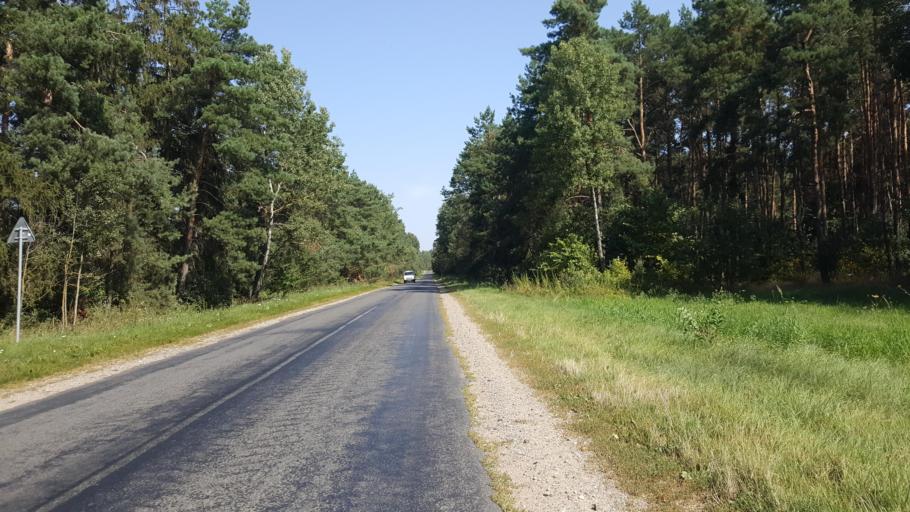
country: BY
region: Brest
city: Vysokaye
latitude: 52.4324
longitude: 23.4449
